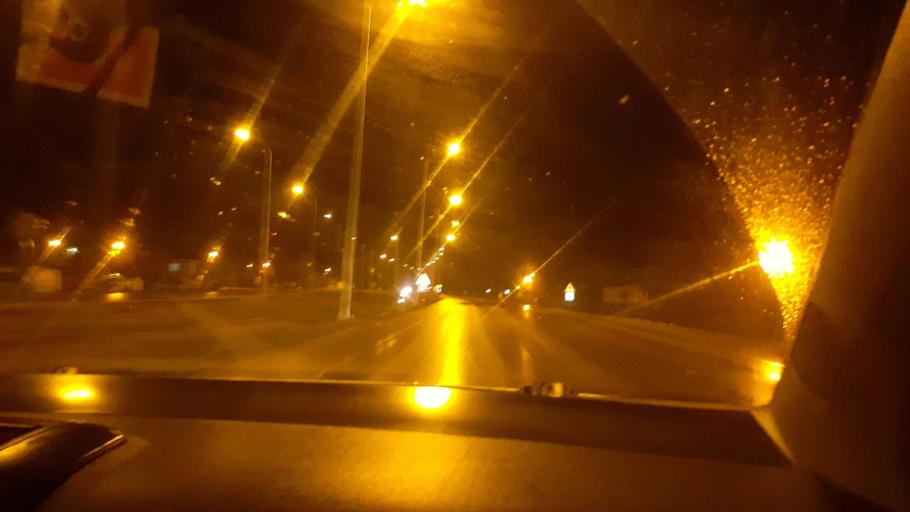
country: TR
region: Hatay
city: Aktepe
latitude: 36.7304
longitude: 36.5236
